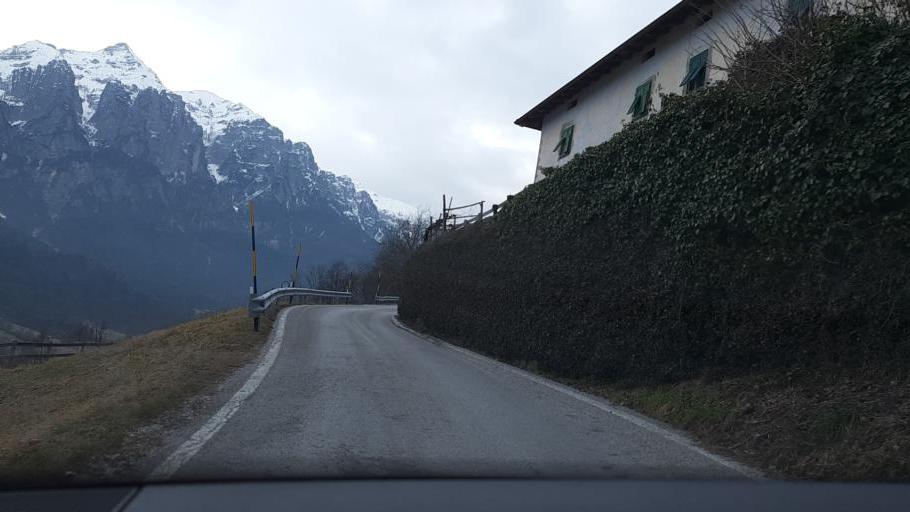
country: IT
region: Trentino-Alto Adige
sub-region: Provincia di Trento
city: Borgo
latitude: 46.0379
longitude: 11.4558
